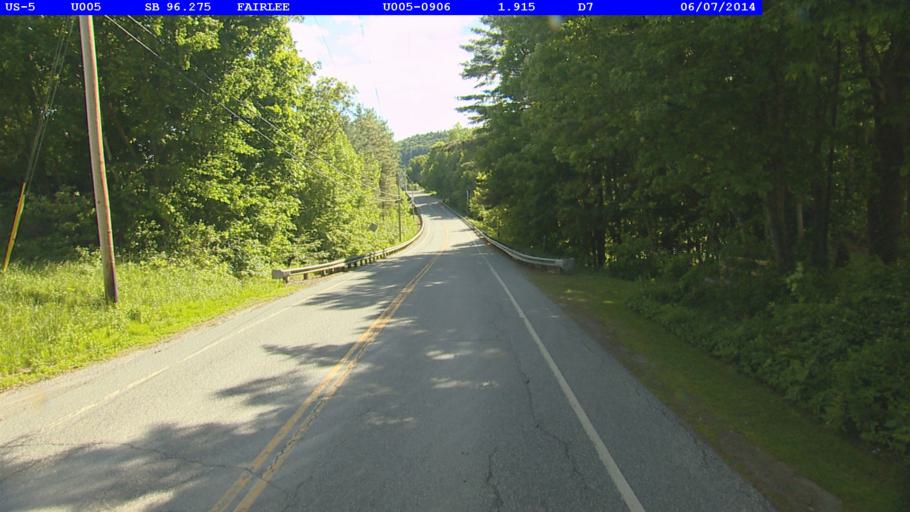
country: US
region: New Hampshire
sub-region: Grafton County
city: Orford
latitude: 43.8977
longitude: -72.1626
